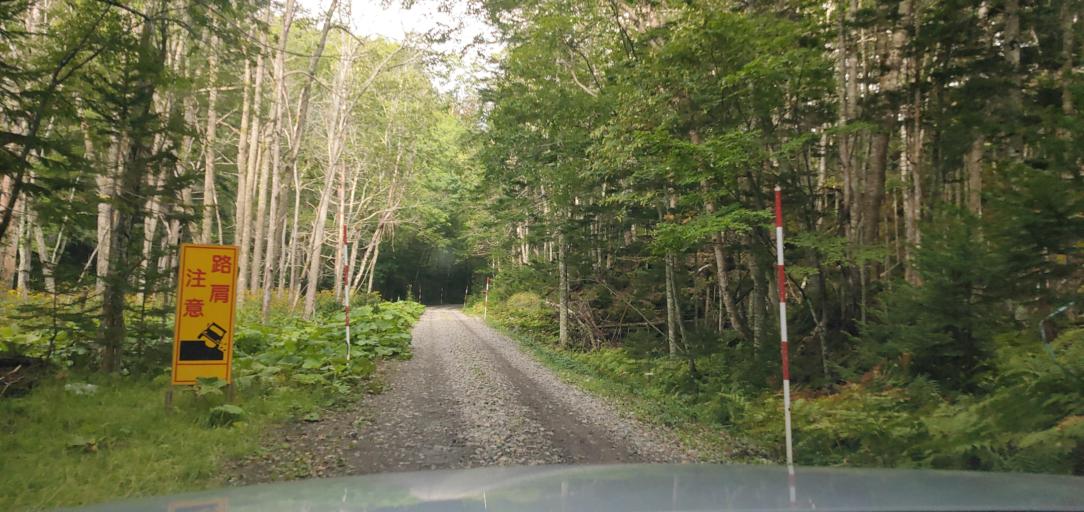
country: JP
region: Hokkaido
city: Kitami
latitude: 43.3715
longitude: 143.9565
